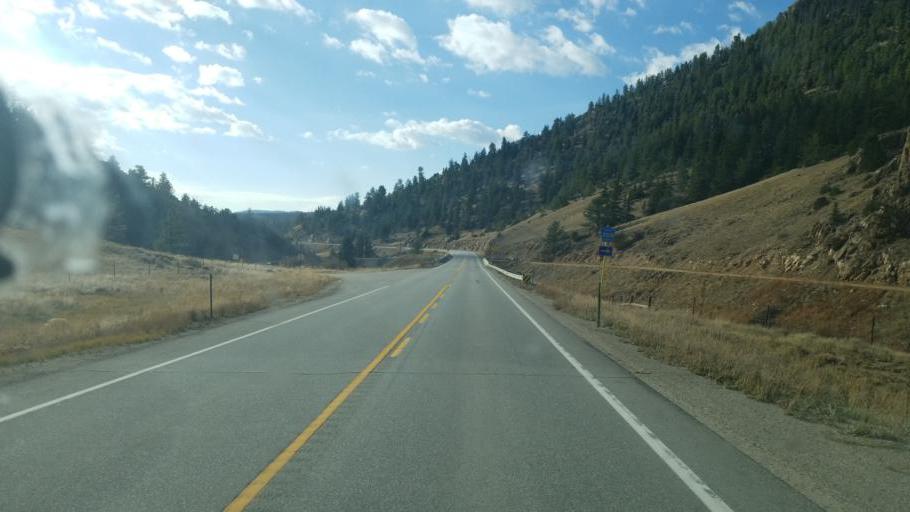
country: US
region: Colorado
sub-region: Chaffee County
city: Buena Vista
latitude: 38.8599
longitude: -105.9863
